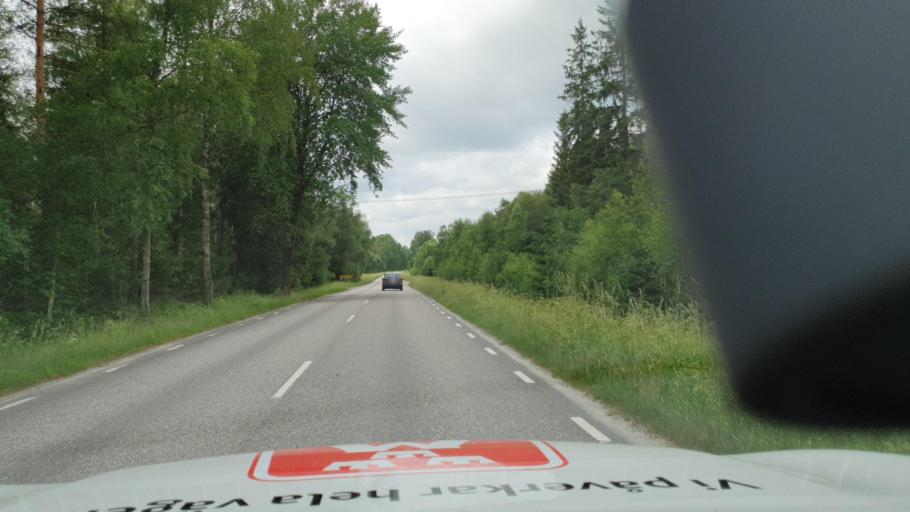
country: SE
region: Vaestra Goetaland
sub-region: Boras Kommun
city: Dalsjofors
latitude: 57.7512
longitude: 13.1600
